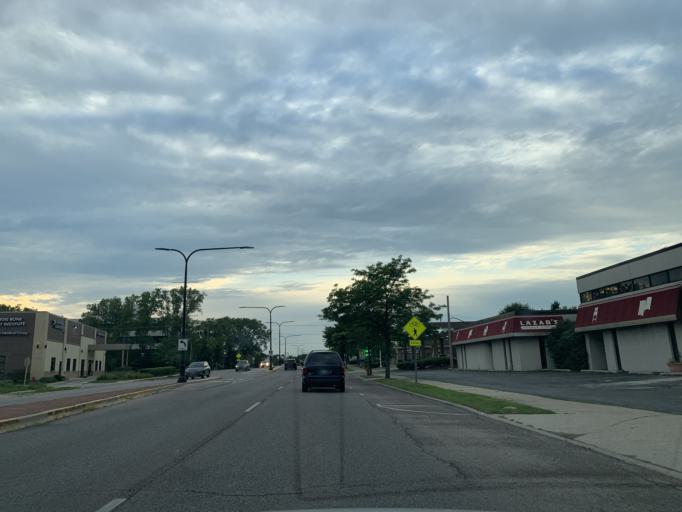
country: US
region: Illinois
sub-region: Cook County
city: Lincolnwood
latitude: 41.9999
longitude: -87.7227
